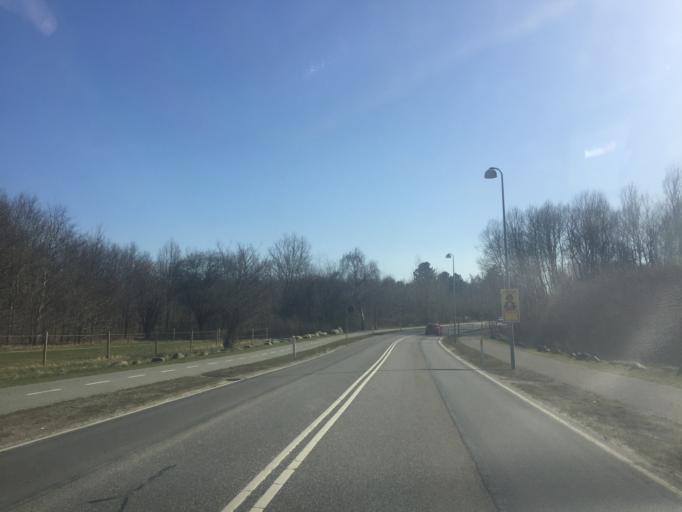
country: DK
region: Capital Region
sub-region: Glostrup Kommune
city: Glostrup
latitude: 55.6888
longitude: 12.4214
